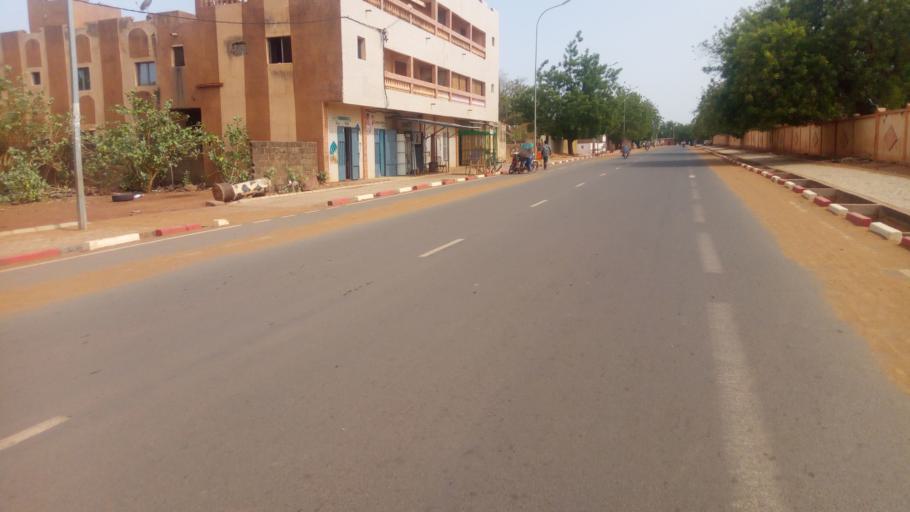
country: ML
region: Segou
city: Segou
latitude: 13.4314
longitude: -6.2888
